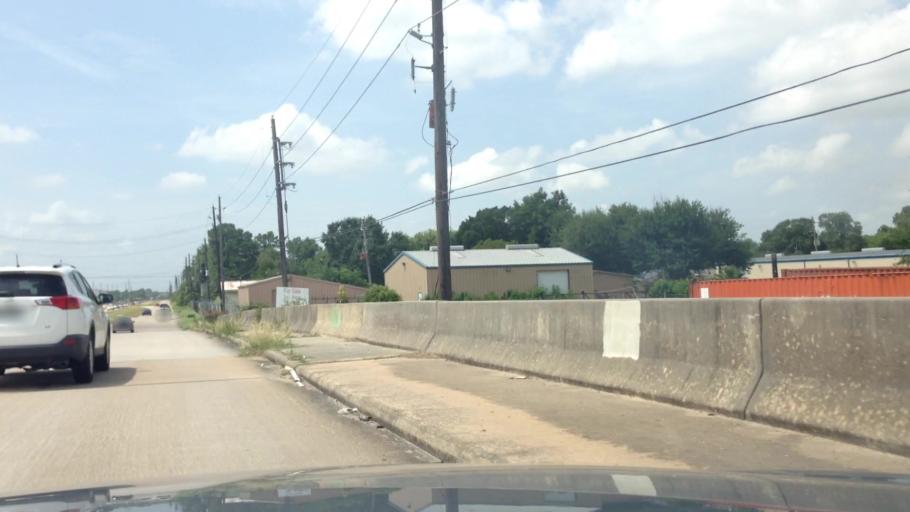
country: US
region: Texas
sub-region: Harris County
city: Jersey Village
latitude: 29.9489
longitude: -95.5470
